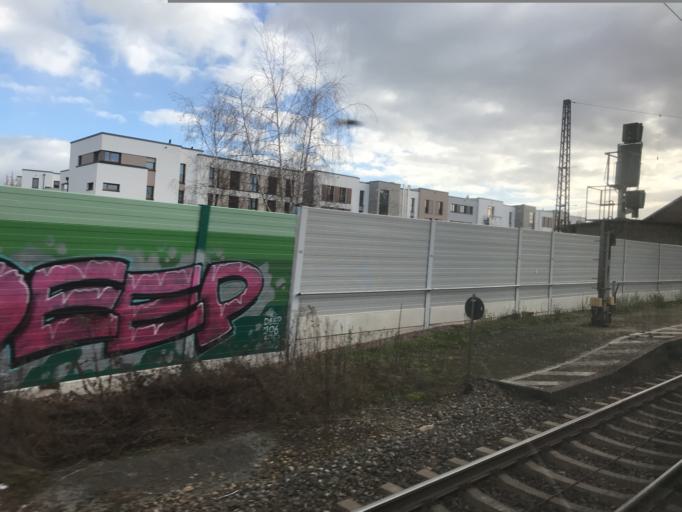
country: DE
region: Baden-Wuerttemberg
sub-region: Freiburg Region
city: Kenzingen
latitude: 48.1964
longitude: 7.7644
